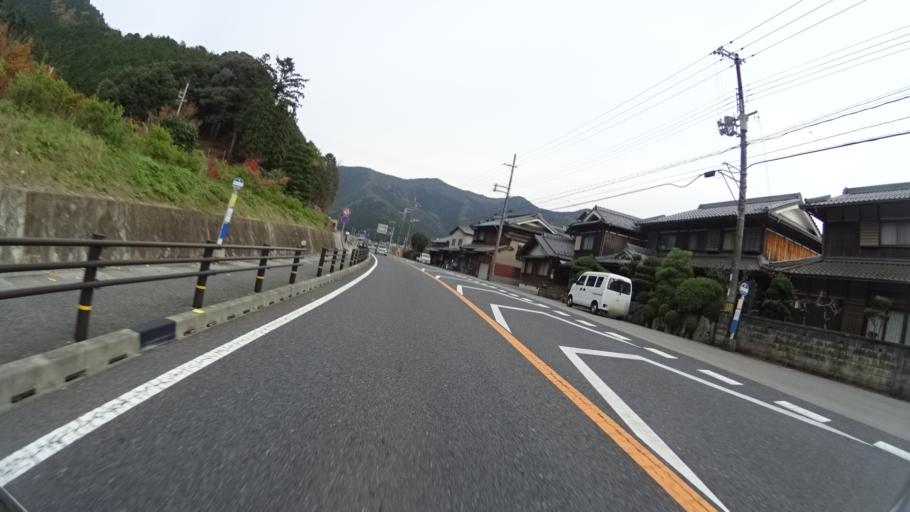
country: JP
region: Hyogo
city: Sasayama
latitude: 35.1179
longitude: 135.0898
